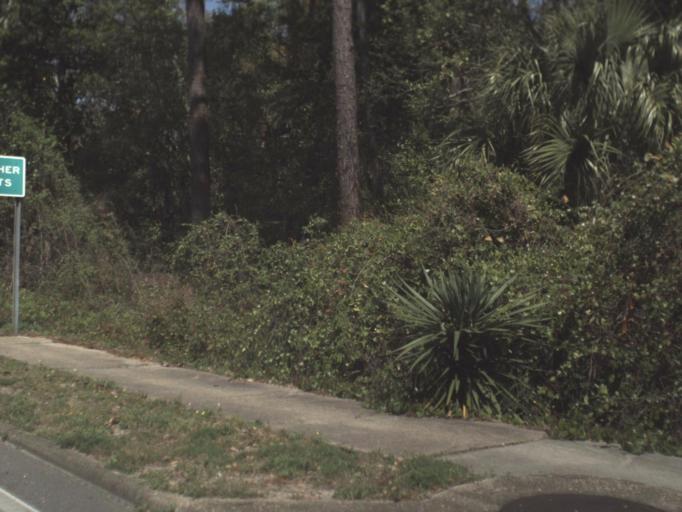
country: US
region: Florida
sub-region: Okaloosa County
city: Fort Walton Beach
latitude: 30.4079
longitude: -86.6407
